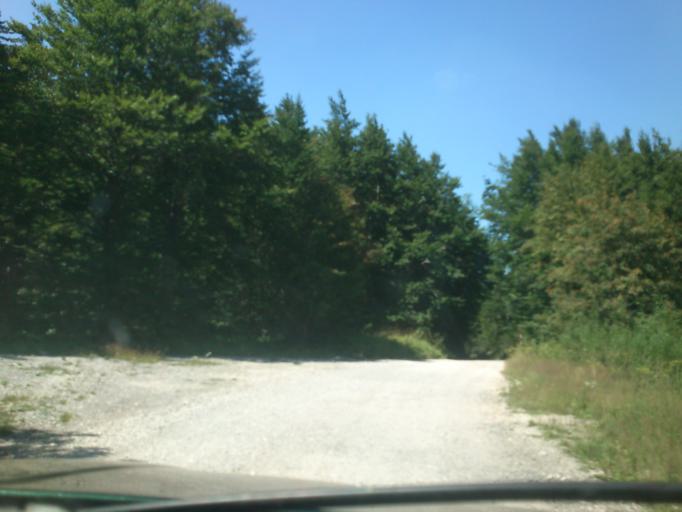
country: HR
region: Licko-Senjska
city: Senj
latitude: 44.8212
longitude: 14.9785
